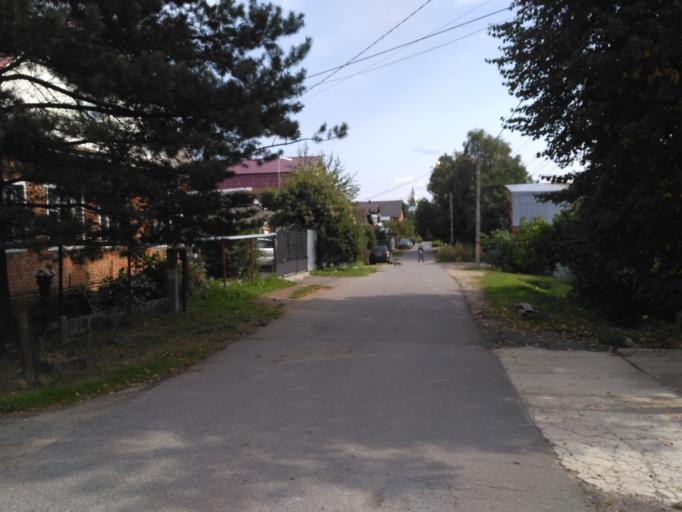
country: RU
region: Moskovskaya
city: Sergiyev Posad
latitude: 56.3149
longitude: 38.1209
